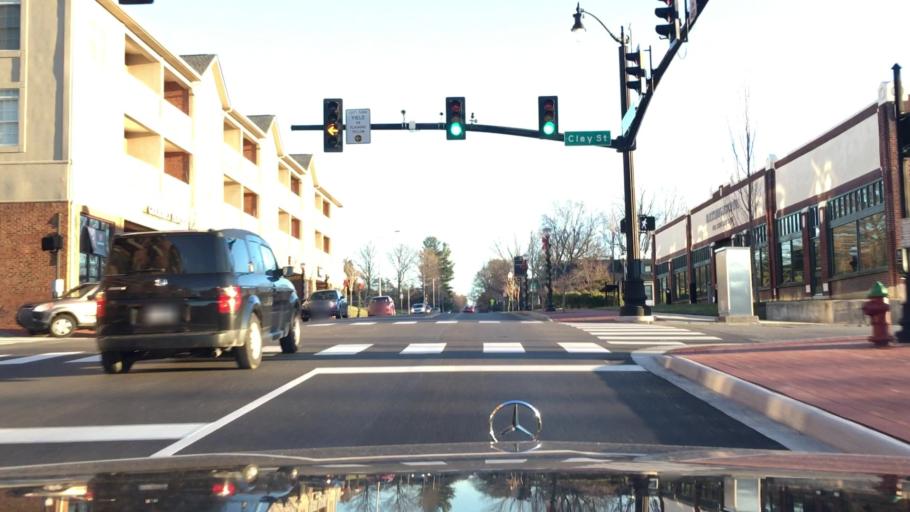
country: US
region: Virginia
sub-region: Montgomery County
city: Blacksburg
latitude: 37.2273
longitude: -80.4119
